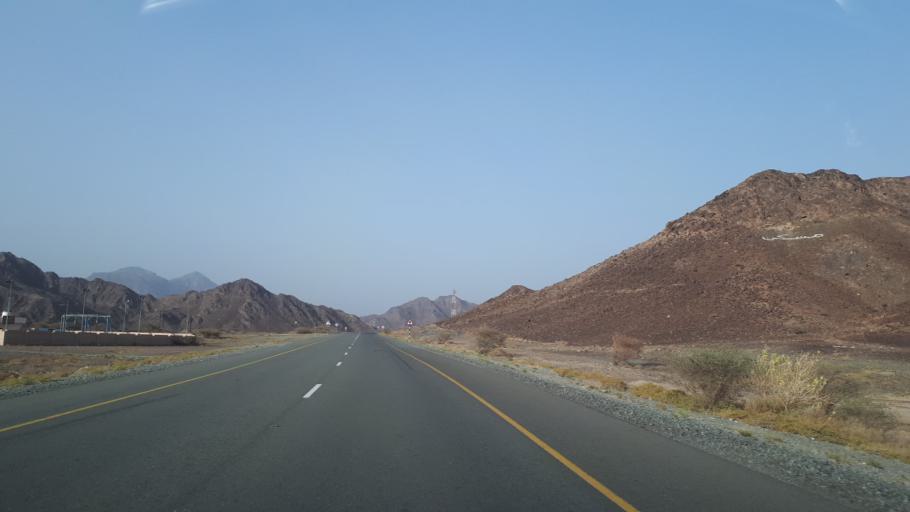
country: OM
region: Az Zahirah
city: Yanqul
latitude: 23.4831
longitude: 56.8106
